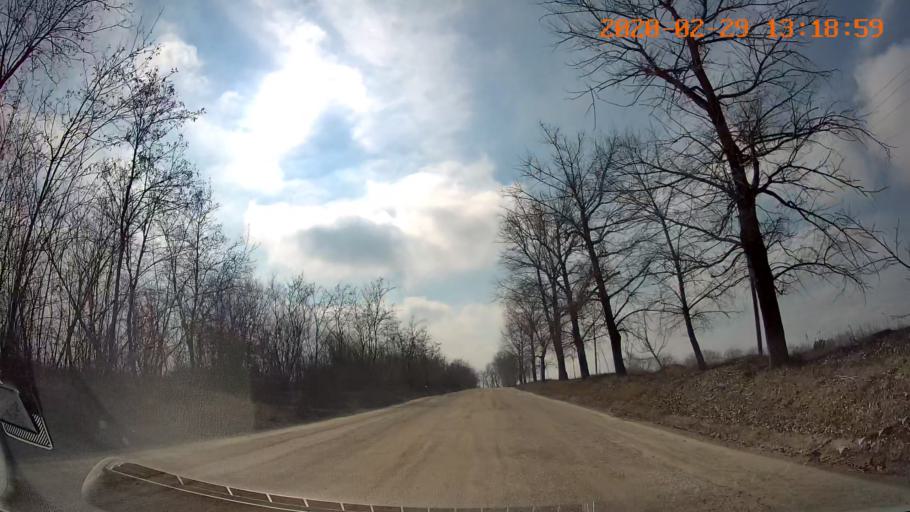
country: MD
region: Telenesti
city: Camenca
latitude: 47.9915
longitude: 28.6542
